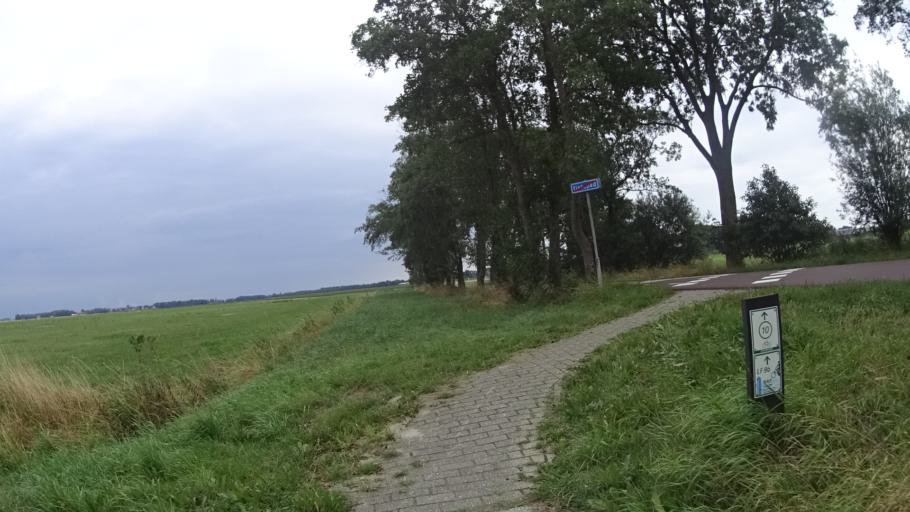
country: NL
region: Groningen
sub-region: Gemeente Slochteren
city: Slochteren
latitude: 53.2063
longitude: 6.8362
